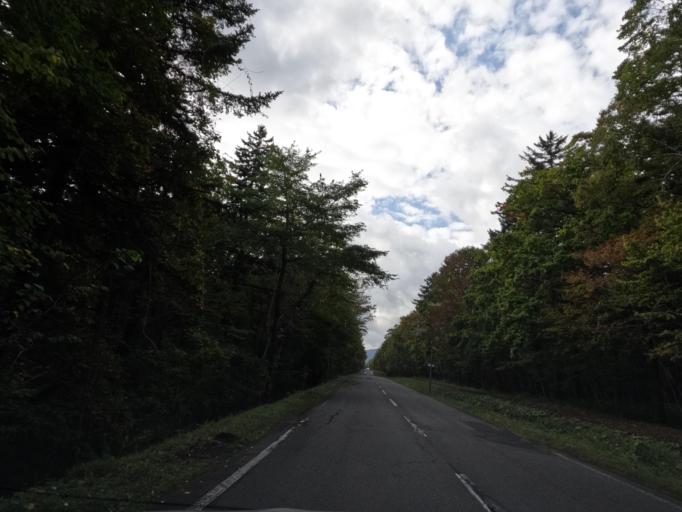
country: JP
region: Hokkaido
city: Chitose
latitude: 42.7919
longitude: 141.5474
